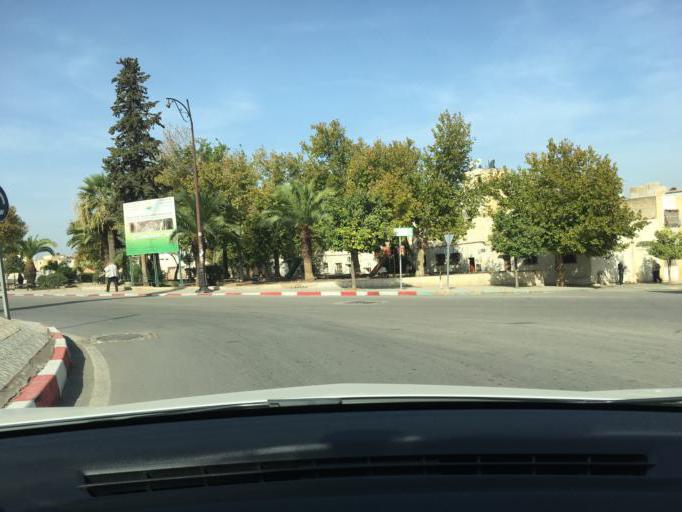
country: MA
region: Fes-Boulemane
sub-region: Fes
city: Fes
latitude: 34.0411
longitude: -5.0144
